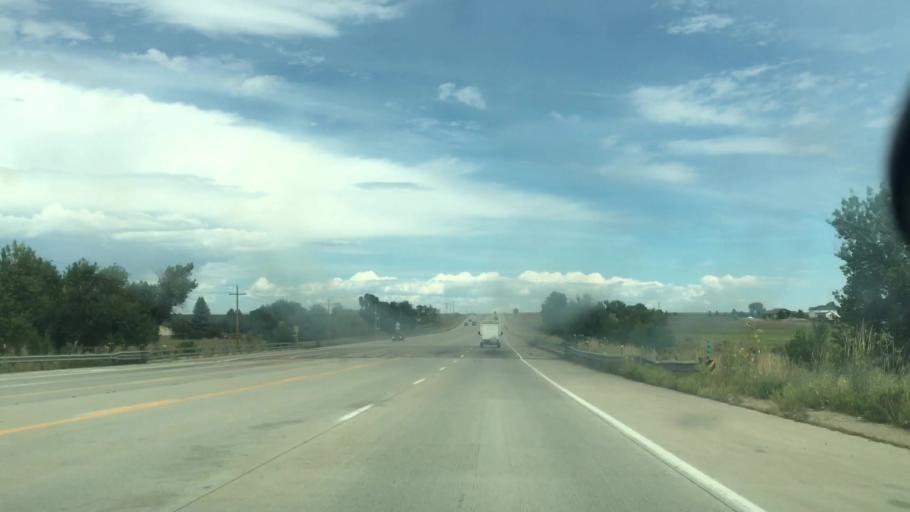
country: US
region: Colorado
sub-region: Larimer County
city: Berthoud
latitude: 40.2767
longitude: -105.1024
